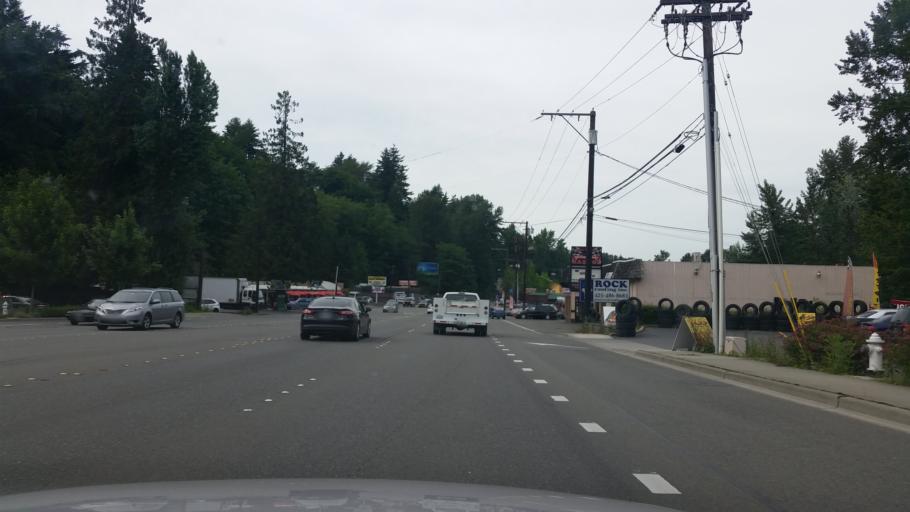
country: US
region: Washington
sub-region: King County
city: Bothell
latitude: 47.7524
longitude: -122.2117
